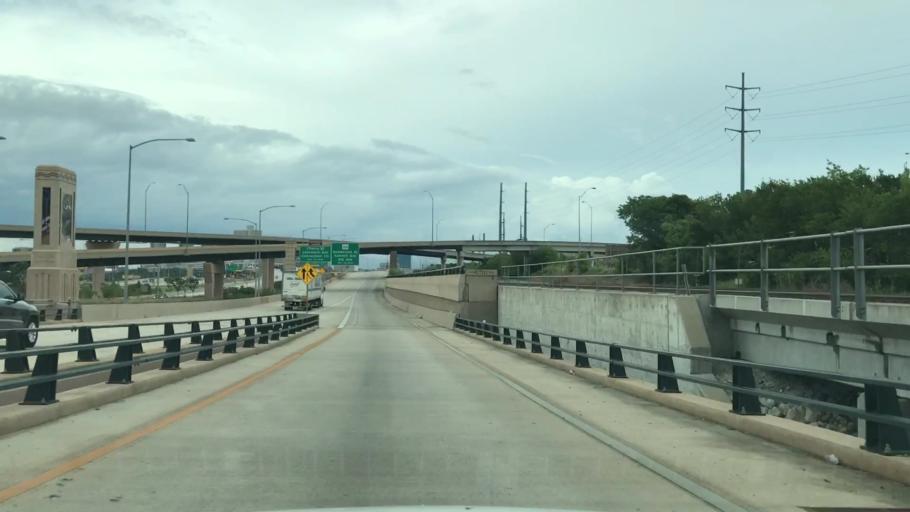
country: US
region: Texas
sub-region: Tarrant County
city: Fort Worth
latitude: 32.7330
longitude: -97.3587
